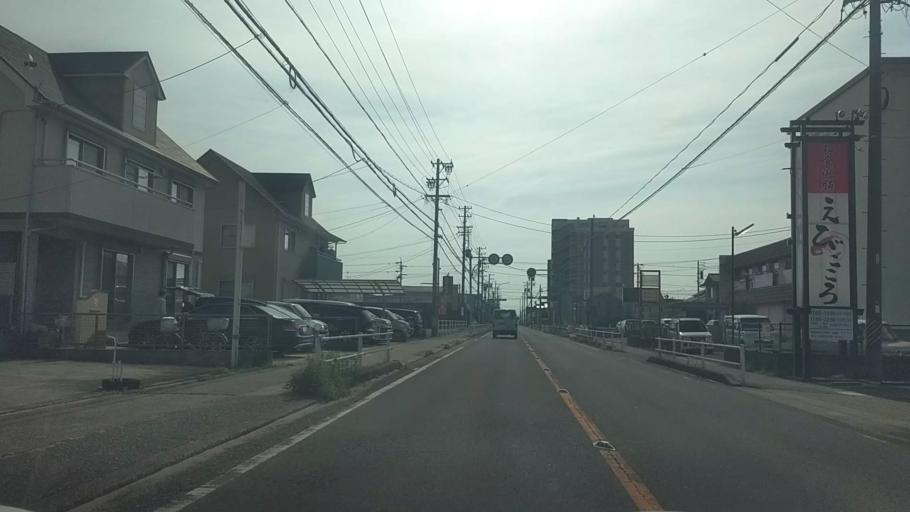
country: JP
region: Aichi
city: Anjo
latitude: 34.9587
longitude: 137.0952
